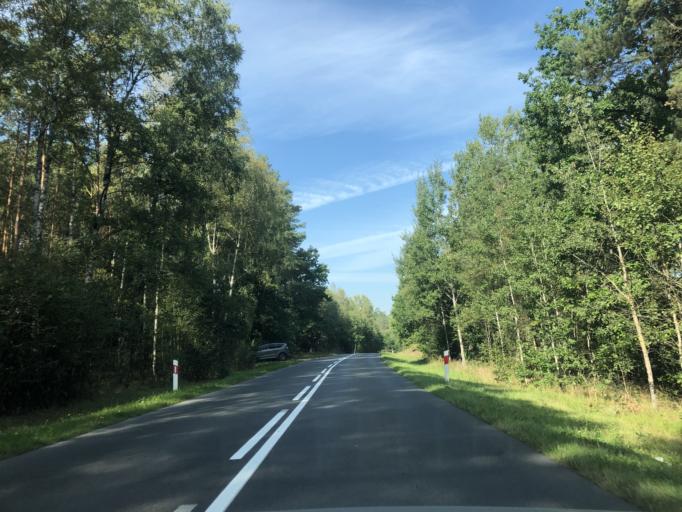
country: PL
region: Greater Poland Voivodeship
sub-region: Powiat pilski
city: Pila
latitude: 53.1277
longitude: 16.8089
